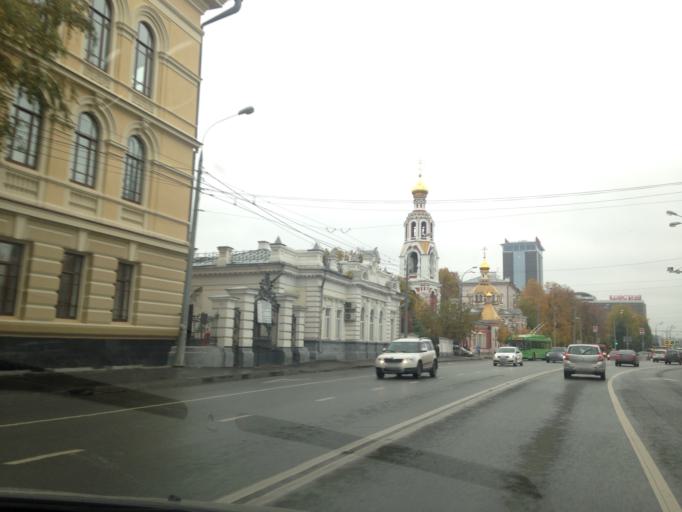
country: RU
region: Tatarstan
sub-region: Gorod Kazan'
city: Kazan
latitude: 55.7947
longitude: 49.1411
